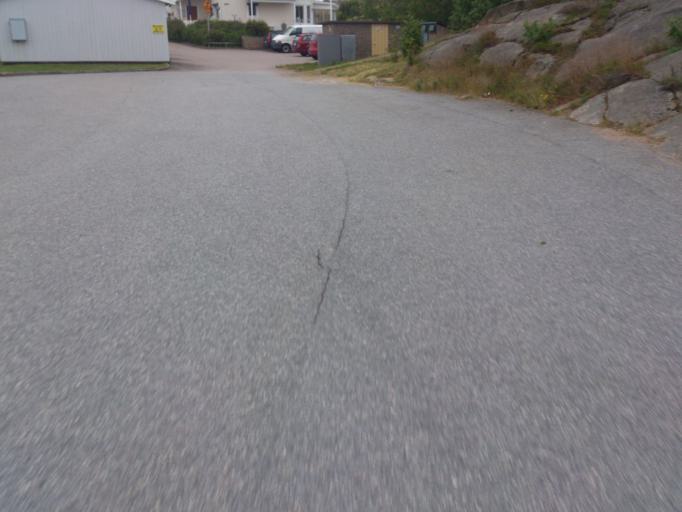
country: SE
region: Vaestra Goetaland
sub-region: Sotenas Kommun
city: Kungshamn
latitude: 58.3776
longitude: 11.2626
